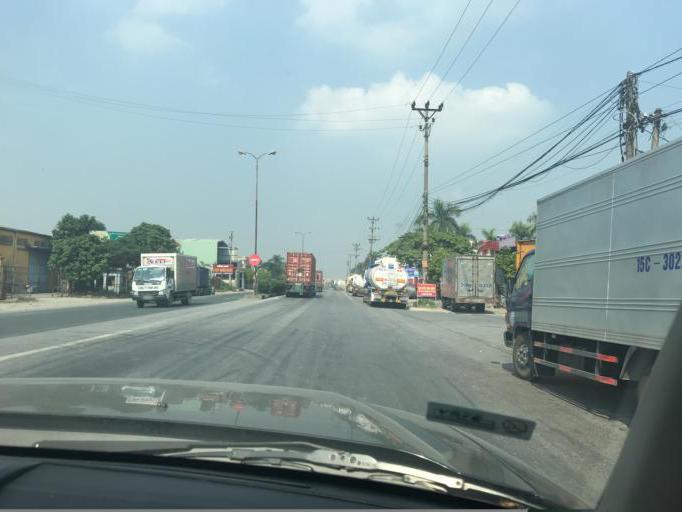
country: VN
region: Hai Phong
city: An Duong
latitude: 20.8761
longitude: 106.6176
